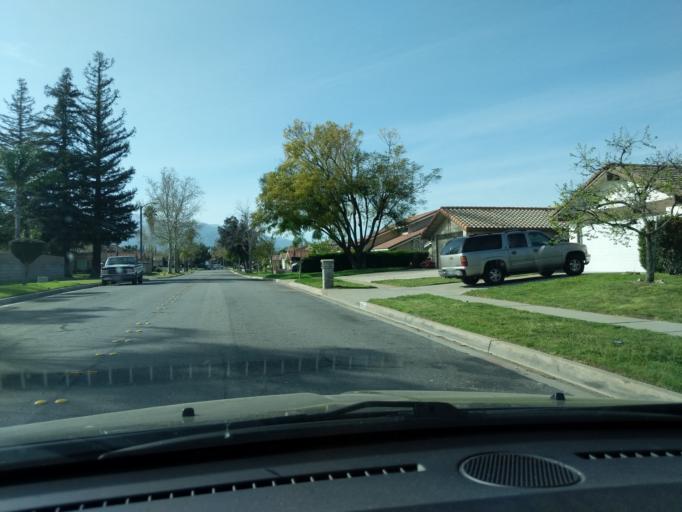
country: US
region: California
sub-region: San Bernardino County
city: Muscoy
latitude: 34.1406
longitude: -117.3684
